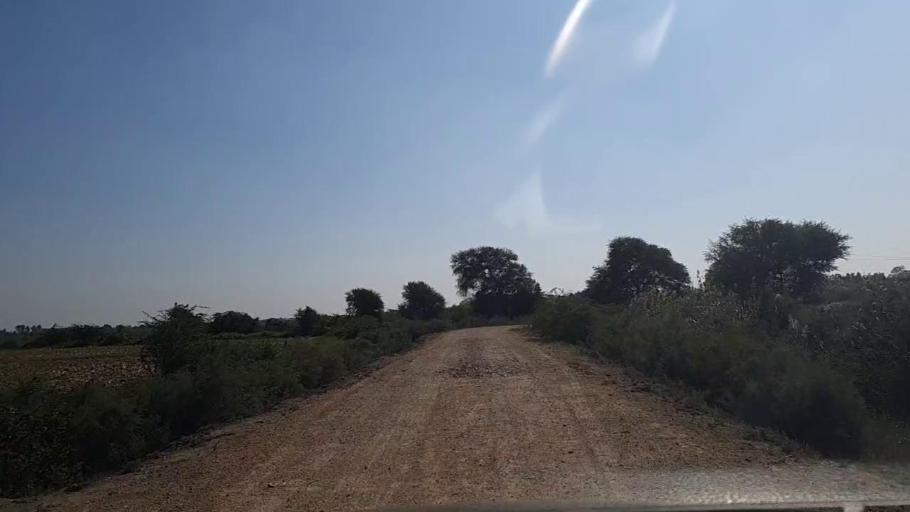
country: PK
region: Sindh
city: Mirpur Batoro
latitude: 24.7311
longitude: 68.2353
